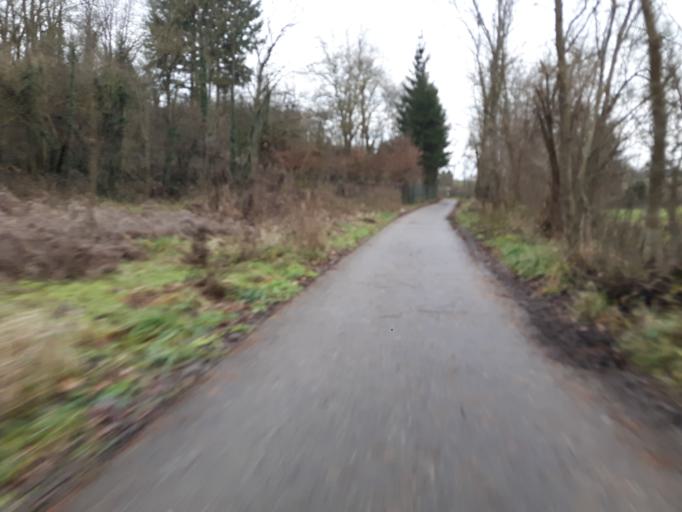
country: DE
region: Baden-Wuerttemberg
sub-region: Regierungsbezirk Stuttgart
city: Flein
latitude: 49.1148
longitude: 9.1988
